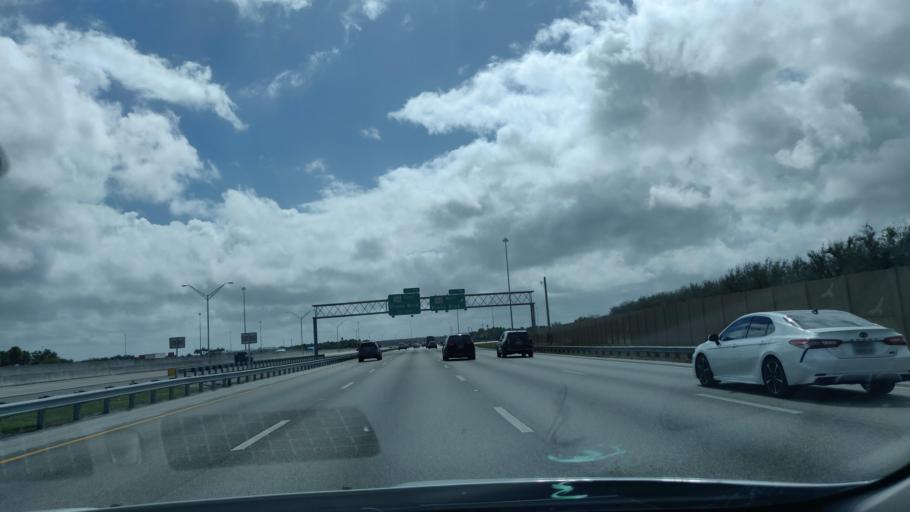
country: US
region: Florida
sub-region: Broward County
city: Sunshine Ranches
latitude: 26.0134
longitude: -80.3444
